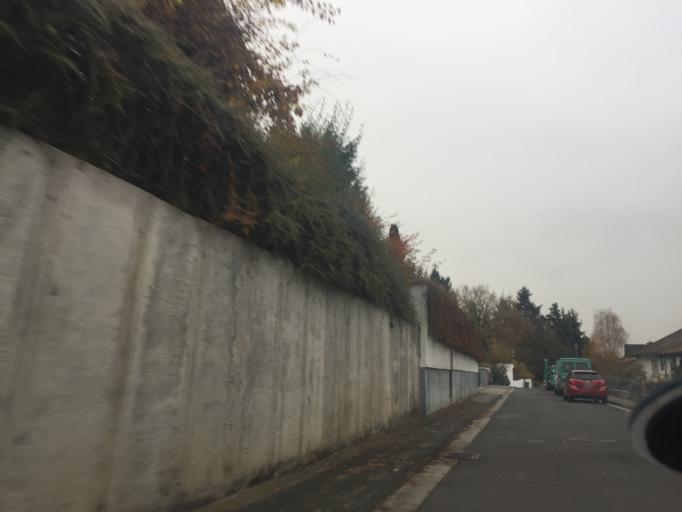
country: DE
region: Hesse
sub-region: Regierungsbezirk Darmstadt
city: Maintal
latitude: 50.1556
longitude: 8.8368
